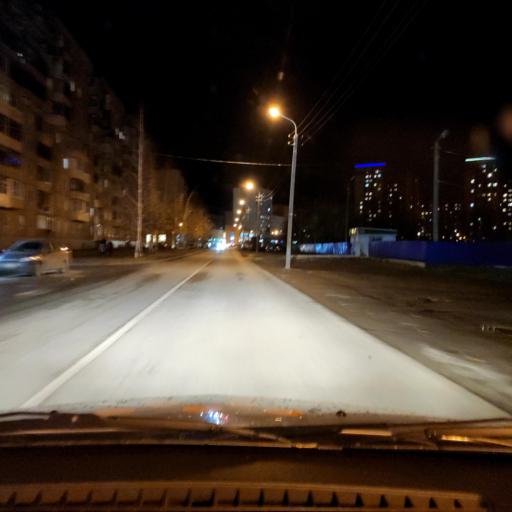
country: RU
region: Bashkortostan
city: Mikhaylovka
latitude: 54.7087
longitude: 55.8387
